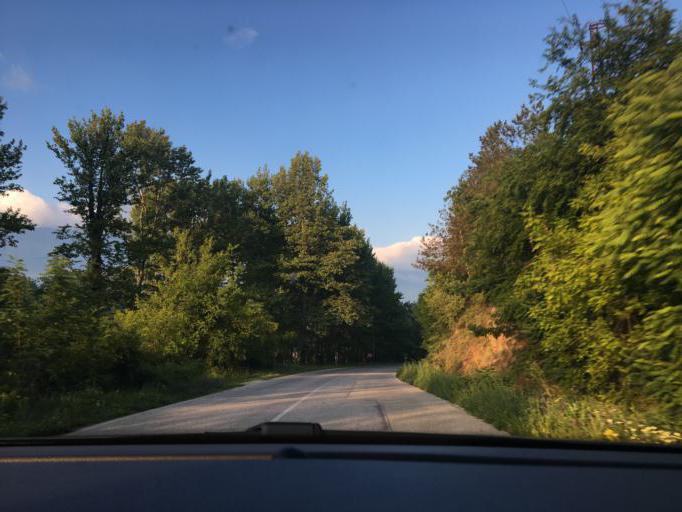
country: MK
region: Novo Selo
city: Novo Selo
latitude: 41.3969
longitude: 23.0284
